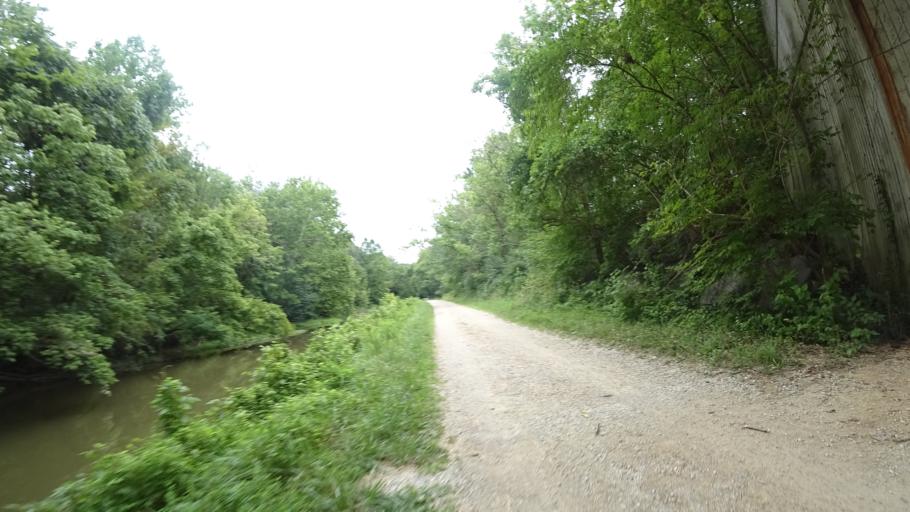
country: US
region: Maryland
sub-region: Montgomery County
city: Travilah
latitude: 39.0386
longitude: -77.2562
